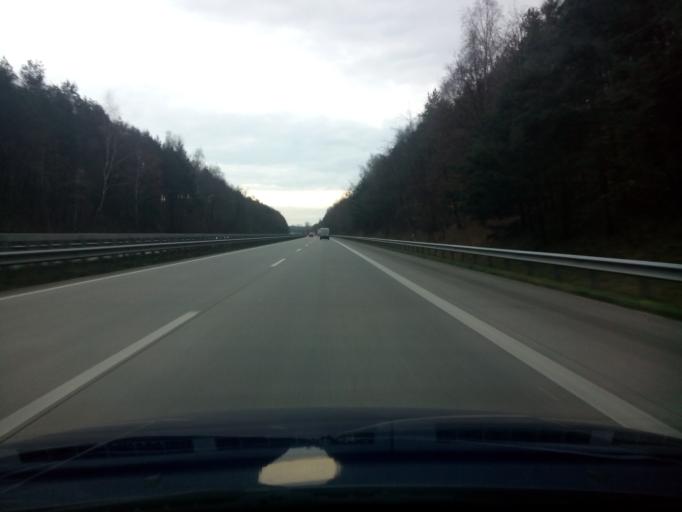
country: DE
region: Lower Saxony
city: Schwanewede
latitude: 53.2421
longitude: 8.6392
